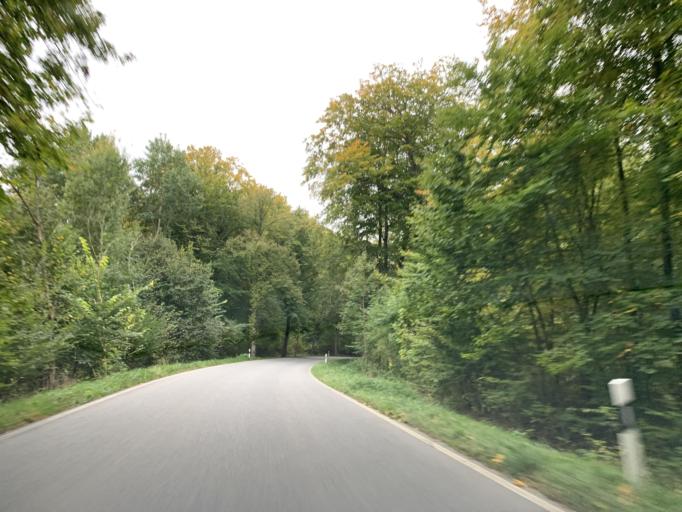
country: DE
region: Mecklenburg-Vorpommern
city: Burg Stargard
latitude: 53.4889
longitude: 13.2994
